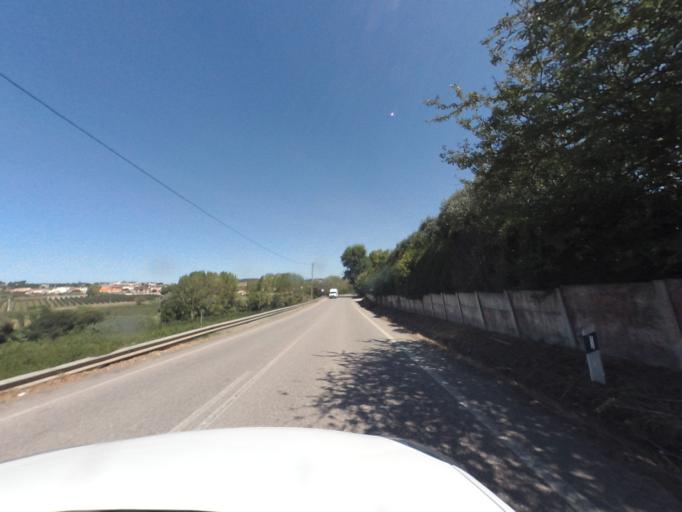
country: PT
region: Leiria
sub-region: Alcobaca
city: Alcobaca
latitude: 39.5209
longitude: -9.0170
